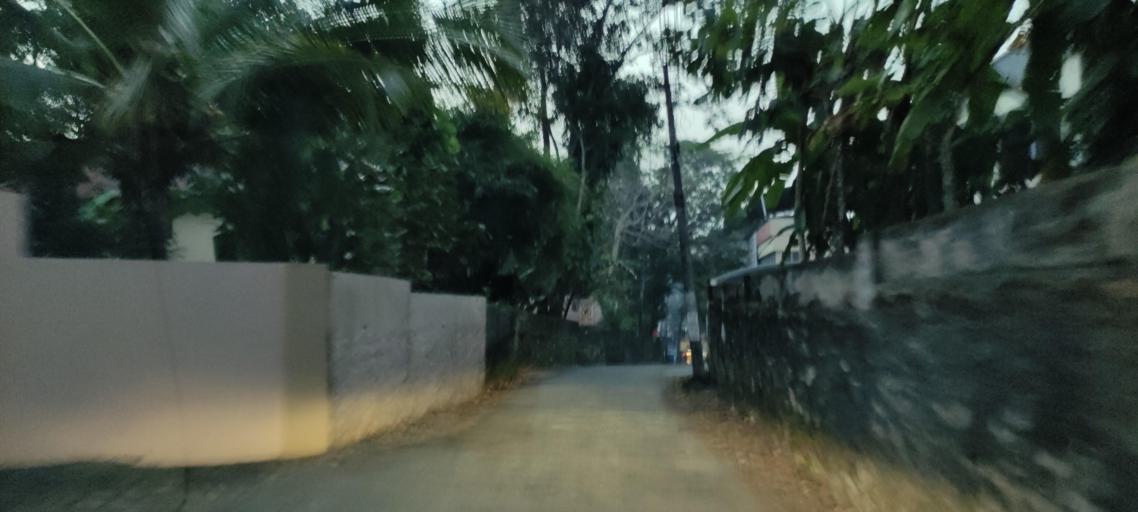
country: IN
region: Kerala
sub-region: Pattanamtitta
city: Adur
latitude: 9.1557
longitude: 76.7334
